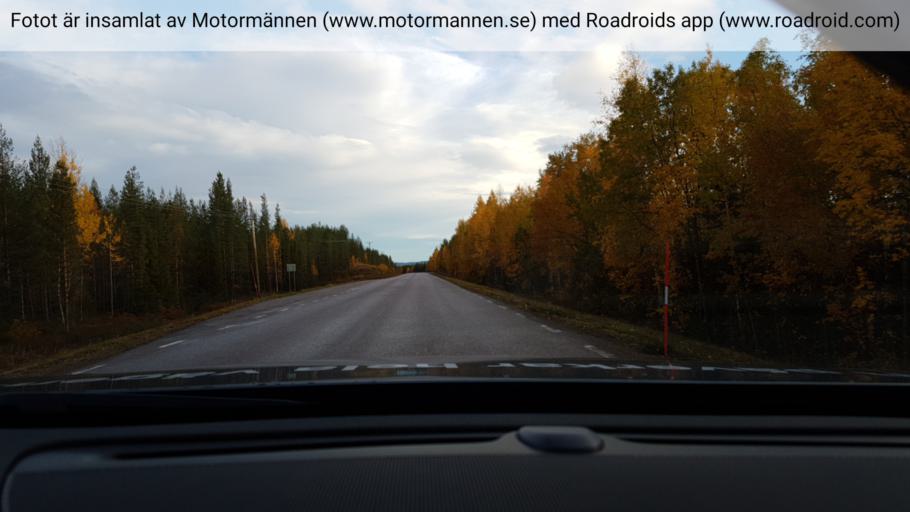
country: SE
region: Norrbotten
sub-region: Overkalix Kommun
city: OEverkalix
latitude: 67.0205
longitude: 22.5205
